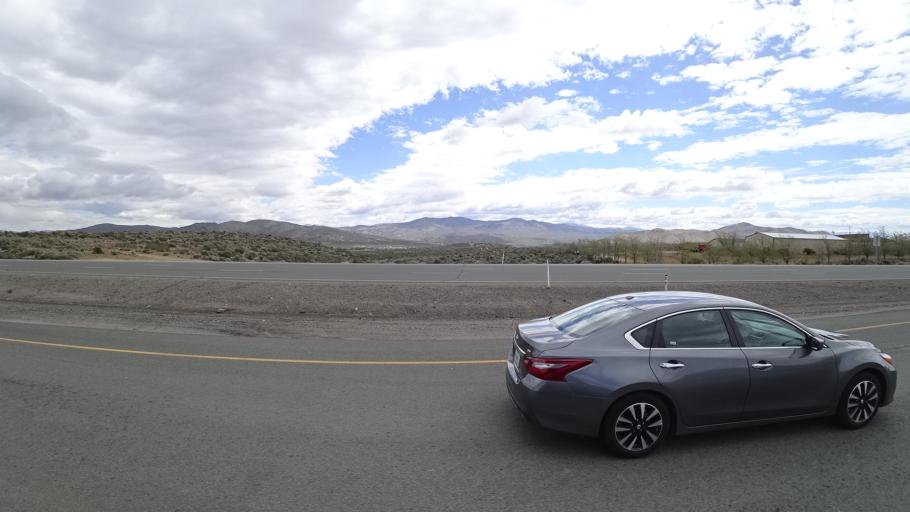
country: US
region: Nevada
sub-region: Douglas County
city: Indian Hills
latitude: 39.1036
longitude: -119.7749
